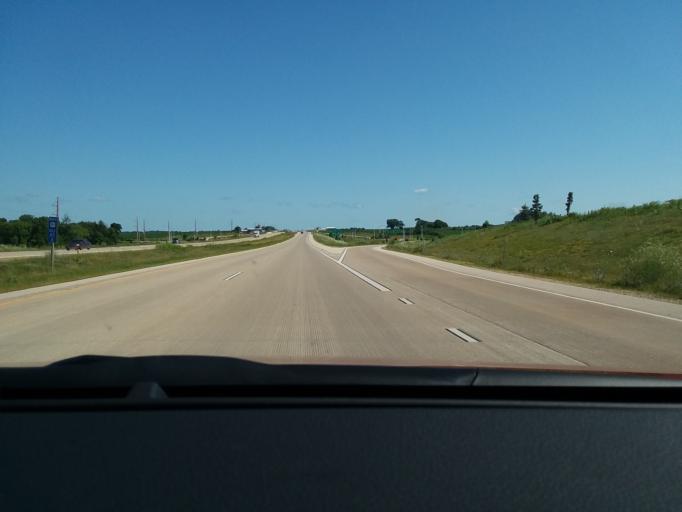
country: US
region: Wisconsin
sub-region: Dane County
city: Windsor
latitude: 43.2114
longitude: -89.3227
